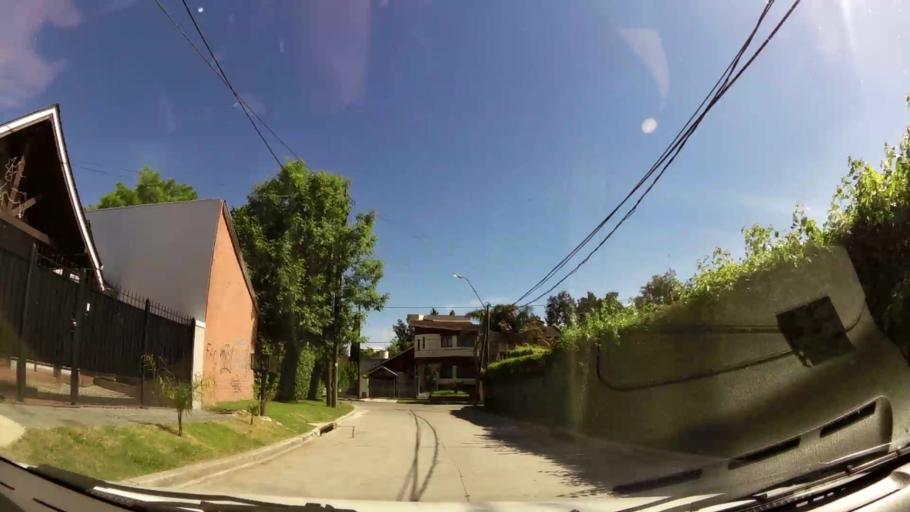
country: AR
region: Buenos Aires
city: Ituzaingo
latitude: -34.6346
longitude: -58.6574
